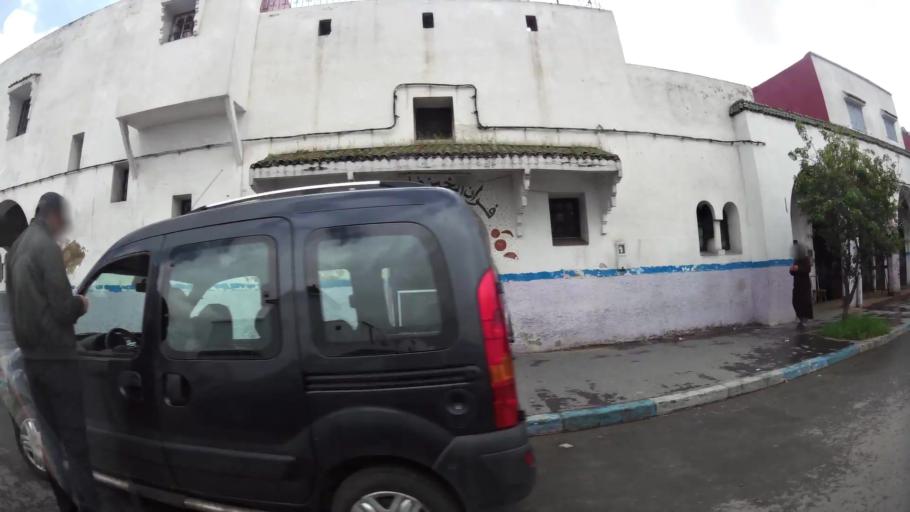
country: MA
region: Grand Casablanca
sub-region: Casablanca
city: Casablanca
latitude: 33.5523
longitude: -7.5988
